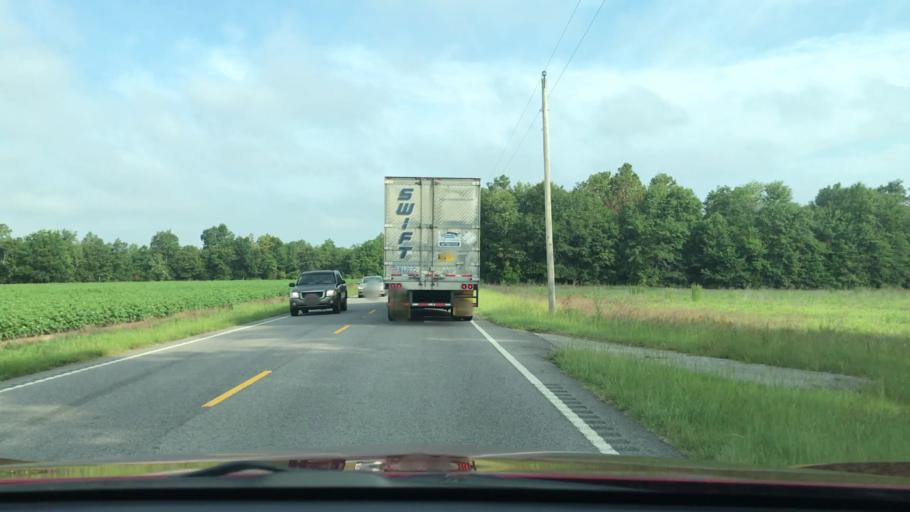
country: US
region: South Carolina
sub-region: Barnwell County
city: Williston
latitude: 33.6263
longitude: -81.2989
